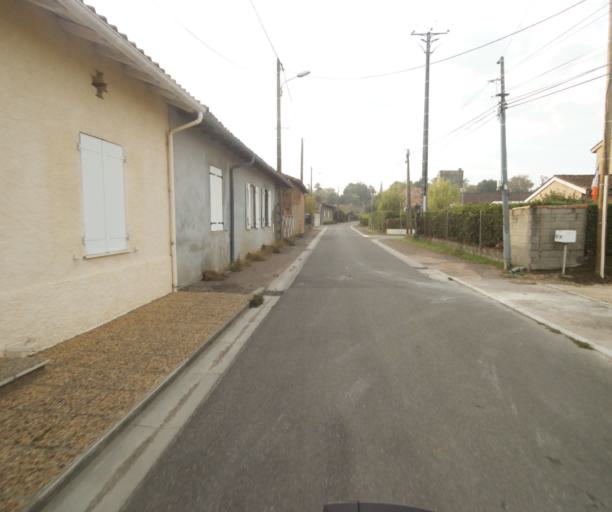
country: FR
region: Midi-Pyrenees
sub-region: Departement du Tarn-et-Garonne
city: Montech
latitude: 43.9614
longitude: 1.2289
